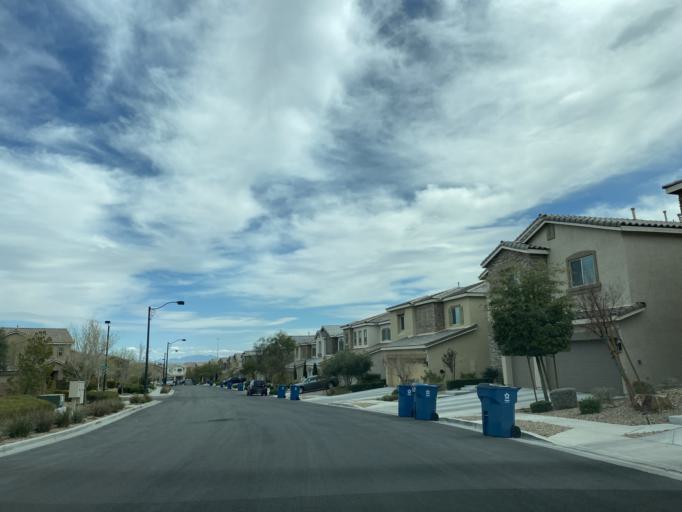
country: US
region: Nevada
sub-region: Clark County
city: Summerlin South
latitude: 36.3071
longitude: -115.2985
